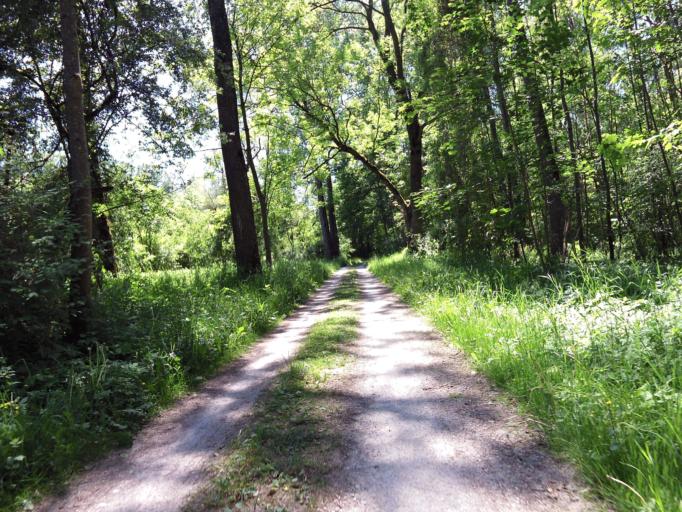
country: DE
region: Bavaria
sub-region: Upper Bavaria
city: Freising
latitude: 48.3714
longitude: 11.7348
